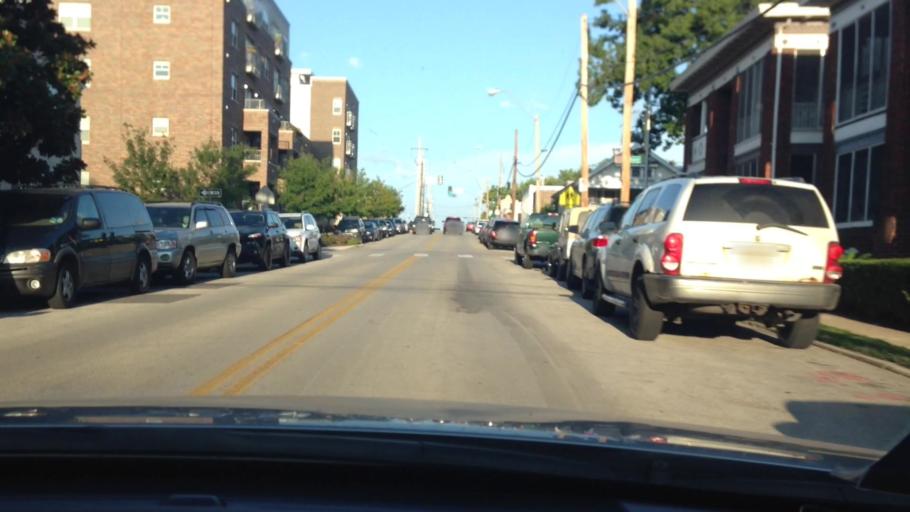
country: US
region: Kansas
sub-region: Johnson County
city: Westwood
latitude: 39.0349
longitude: -94.5890
